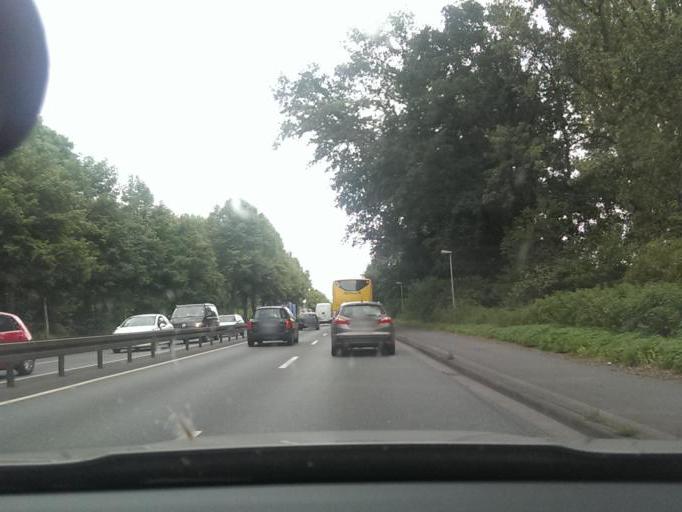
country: DE
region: Lower Saxony
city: Auf der Horst
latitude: 52.4115
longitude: 9.6500
